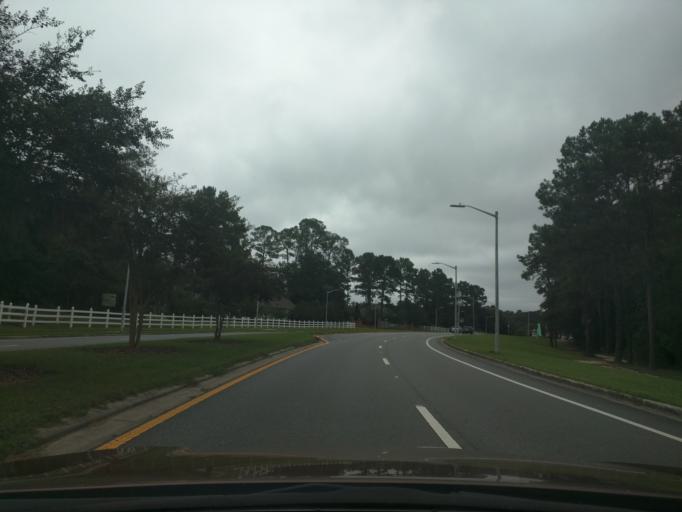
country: US
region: Florida
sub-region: Leon County
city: Tallahassee
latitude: 30.4393
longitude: -84.2033
